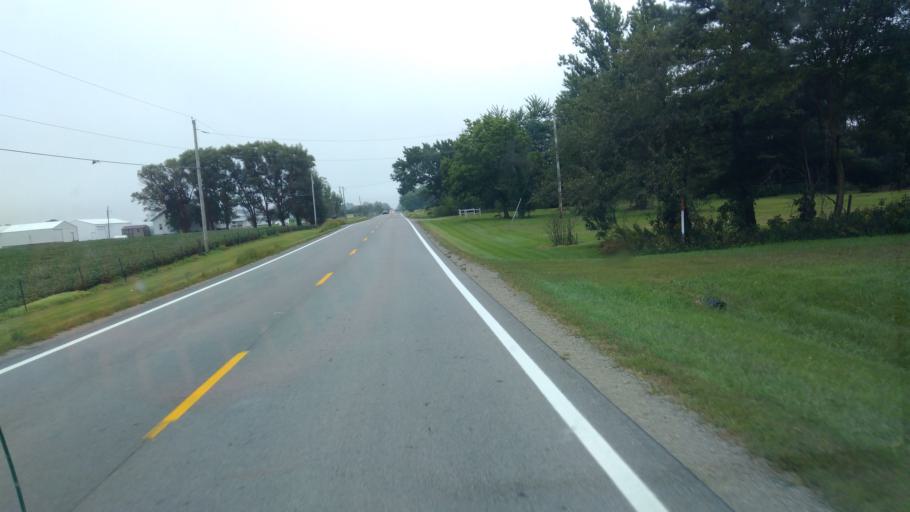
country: US
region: Ohio
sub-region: Union County
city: Richwood
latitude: 40.4767
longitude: -83.4747
